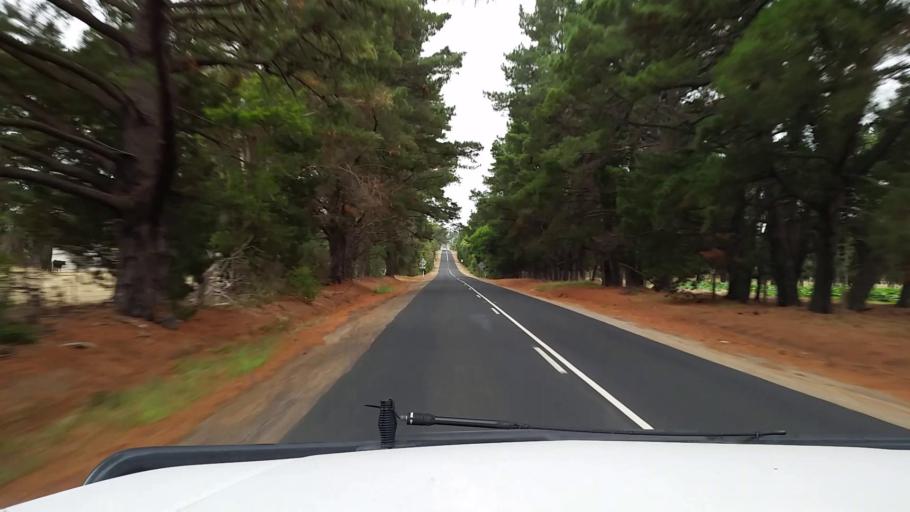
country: AU
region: Victoria
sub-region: Mornington Peninsula
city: Balnarring
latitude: -38.3508
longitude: 145.1457
